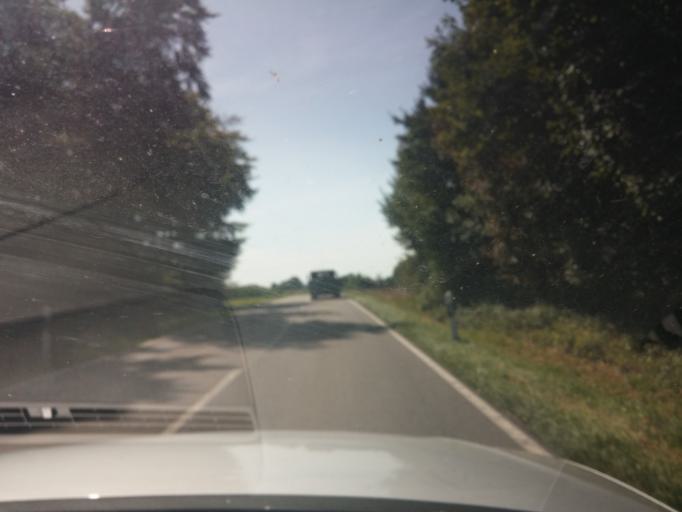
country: DE
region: Baden-Wuerttemberg
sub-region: Tuebingen Region
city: Ertingen
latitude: 48.0688
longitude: 9.4885
